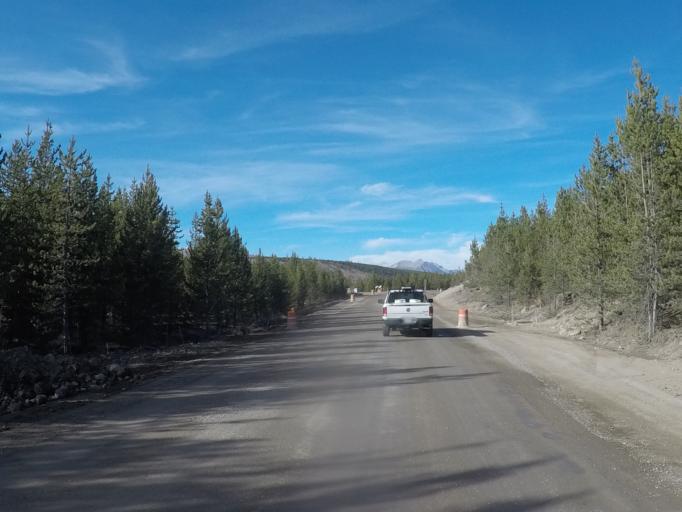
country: US
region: Montana
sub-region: Gallatin County
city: West Yellowstone
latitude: 44.8371
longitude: -110.7316
